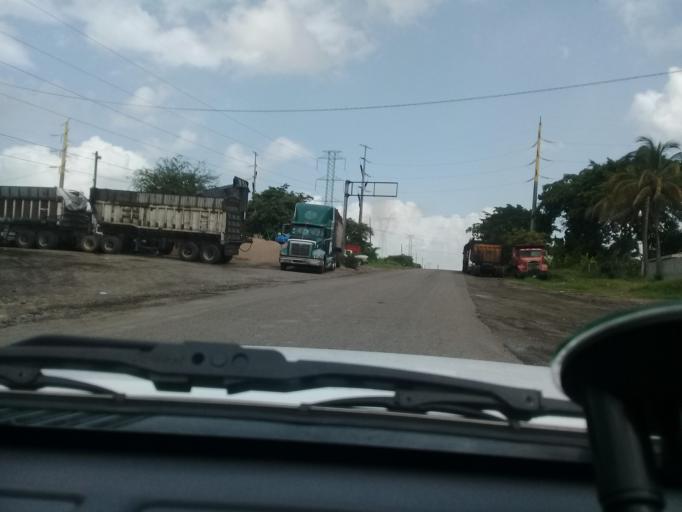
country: MX
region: Veracruz
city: Moralillo
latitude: 22.2181
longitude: -98.0014
